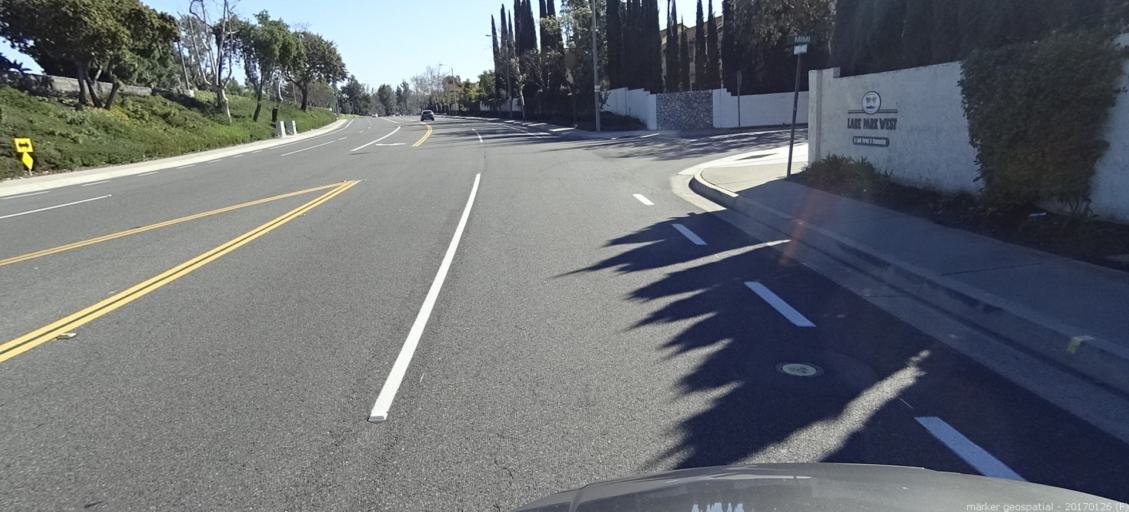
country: US
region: California
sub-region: Orange County
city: Lake Forest
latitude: 33.6446
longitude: -117.7101
